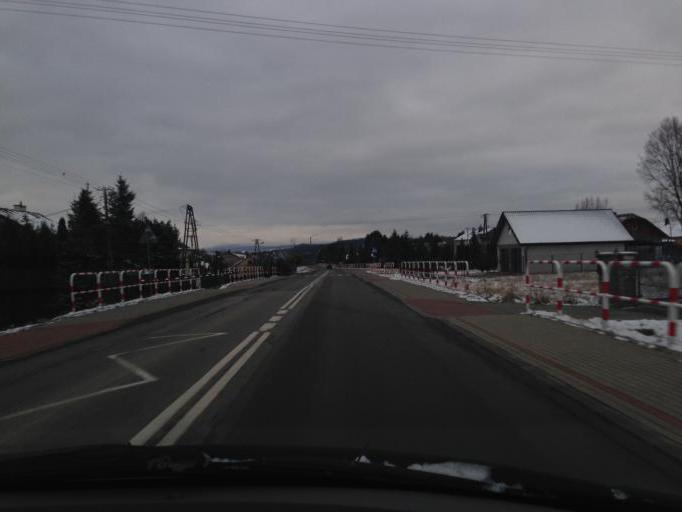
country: PL
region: Lesser Poland Voivodeship
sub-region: Powiat gorlicki
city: Gorlice
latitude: 49.7048
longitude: 21.1370
